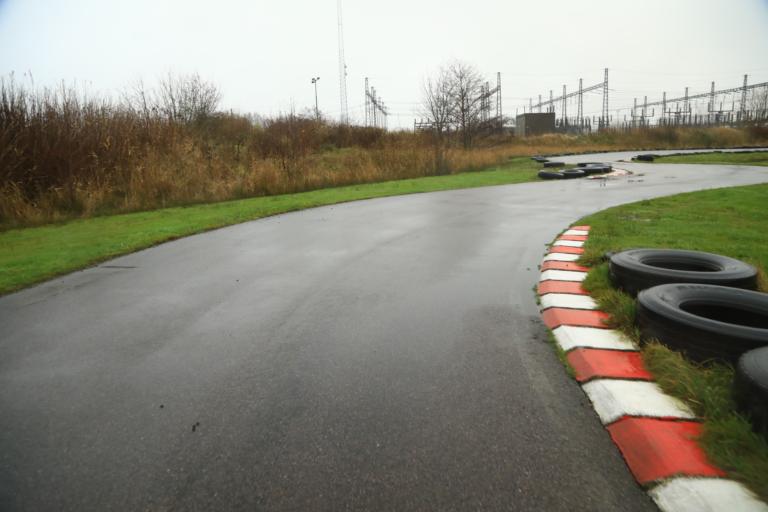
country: SE
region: Halland
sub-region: Varbergs Kommun
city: Varberg
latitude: 57.1270
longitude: 12.3006
